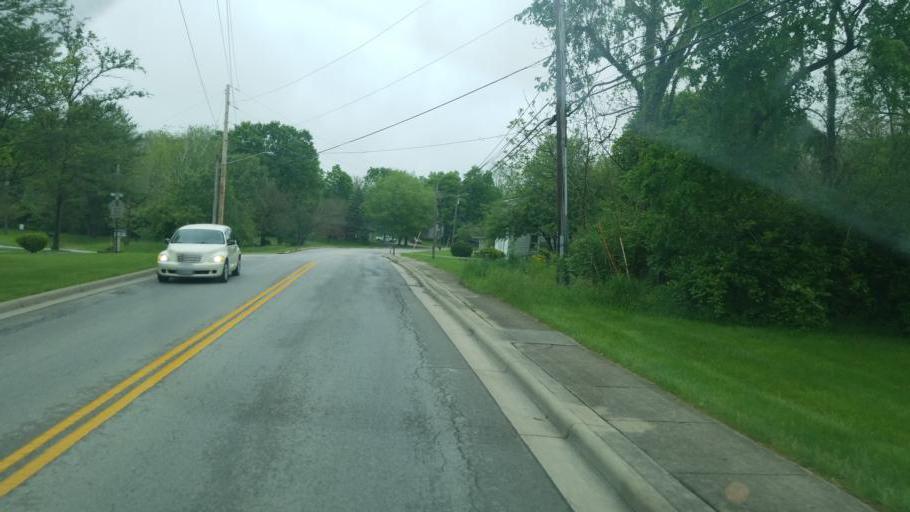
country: US
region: Ohio
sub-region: Highland County
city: Hillsboro
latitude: 39.2139
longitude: -83.6135
